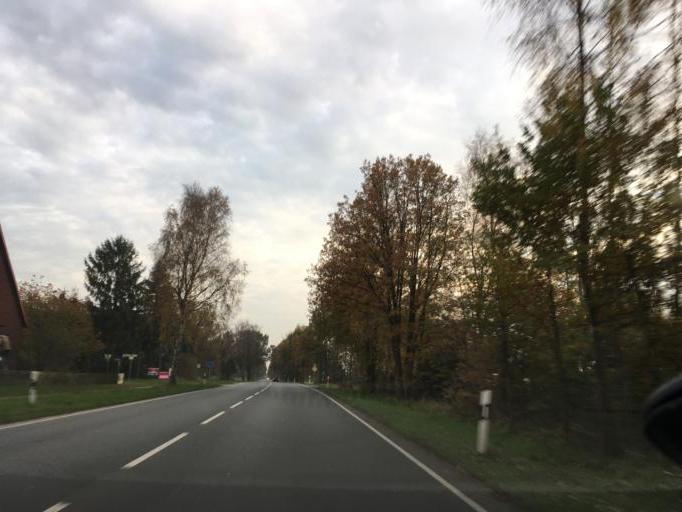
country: DE
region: Lower Saxony
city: Bergen
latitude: 52.7906
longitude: 9.9721
